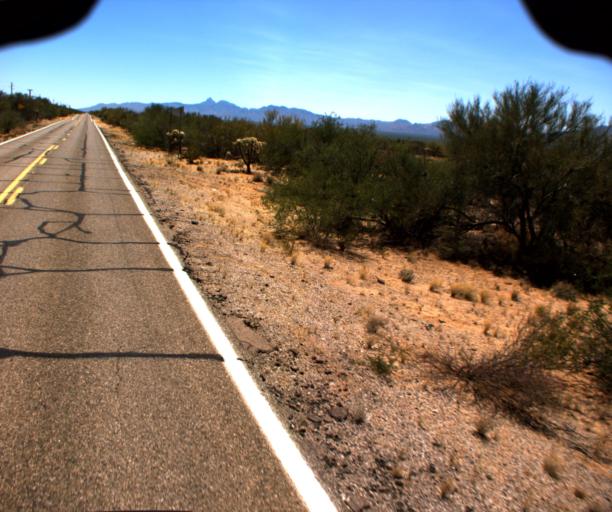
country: US
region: Arizona
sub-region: Pima County
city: Three Points
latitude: 32.0118
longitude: -111.3544
